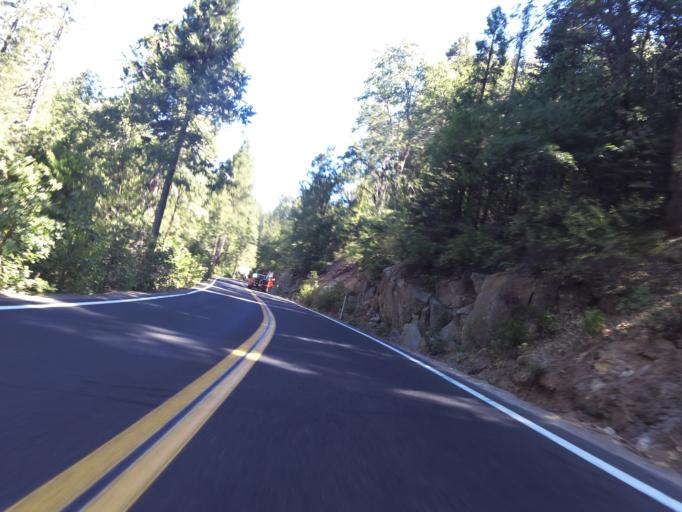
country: US
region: California
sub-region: Calaveras County
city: Arnold
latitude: 38.2710
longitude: -120.3216
